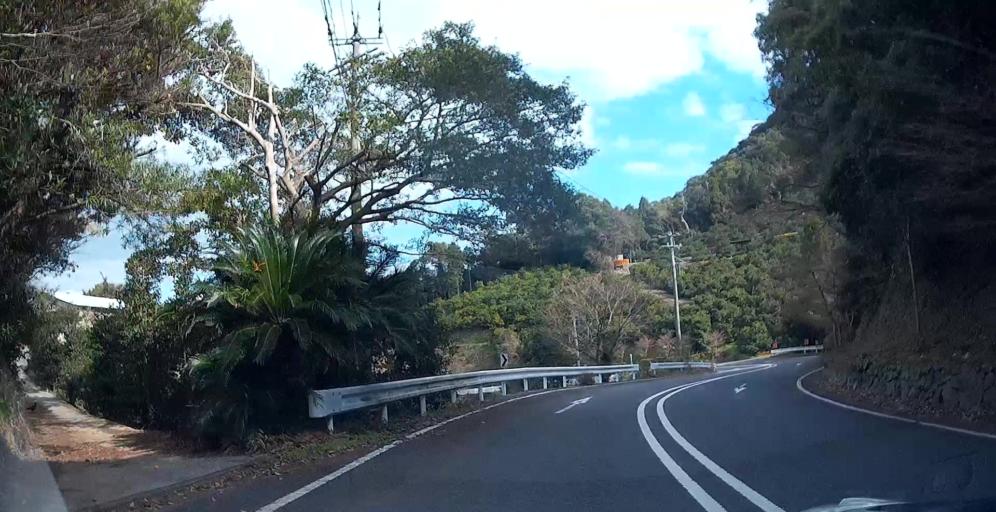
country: JP
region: Kumamoto
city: Minamata
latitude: 32.3251
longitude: 130.4730
